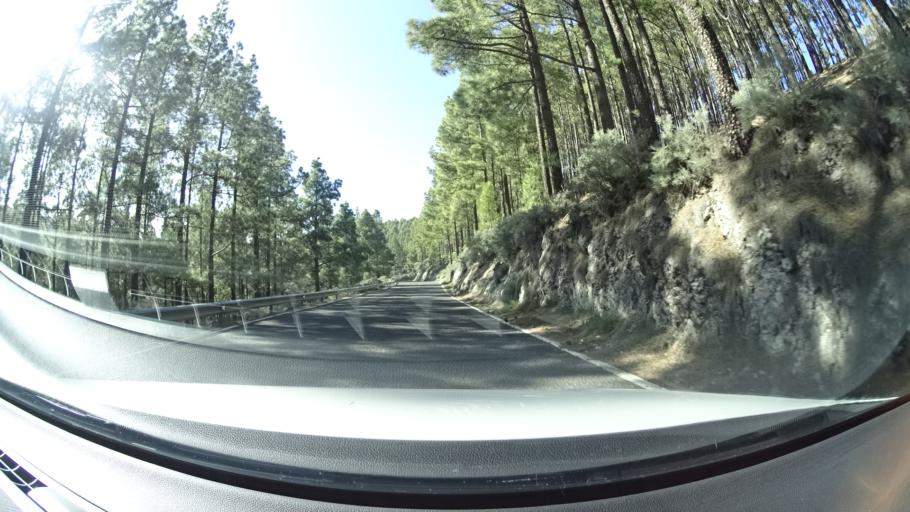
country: ES
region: Canary Islands
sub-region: Provincia de Las Palmas
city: Vega de San Mateo
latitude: 27.9658
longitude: -15.5434
